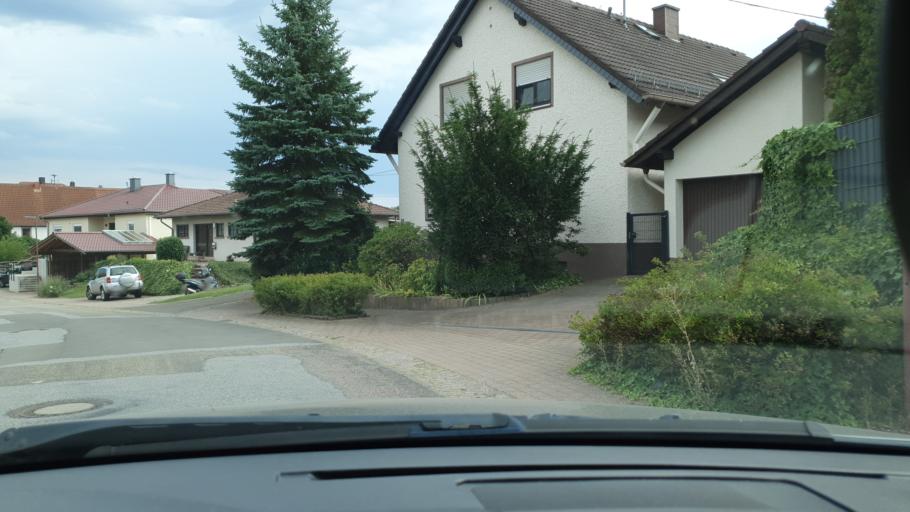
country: DE
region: Rheinland-Pfalz
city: Knopp-Labach
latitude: 49.3333
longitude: 7.5066
